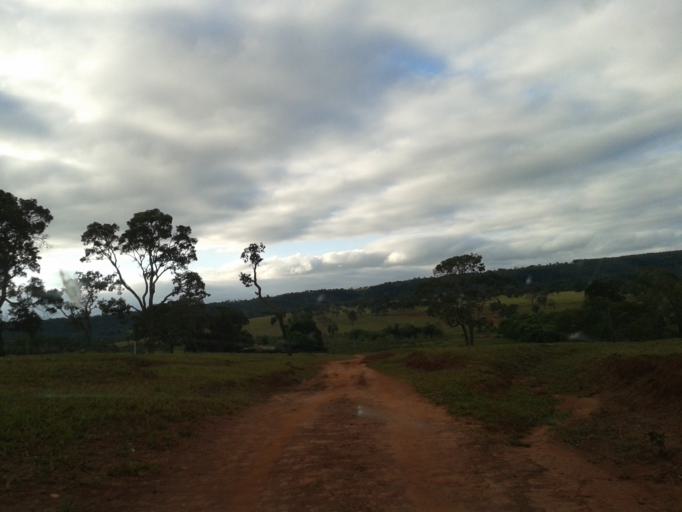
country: BR
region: Minas Gerais
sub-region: Campina Verde
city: Campina Verde
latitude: -19.4763
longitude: -49.6518
